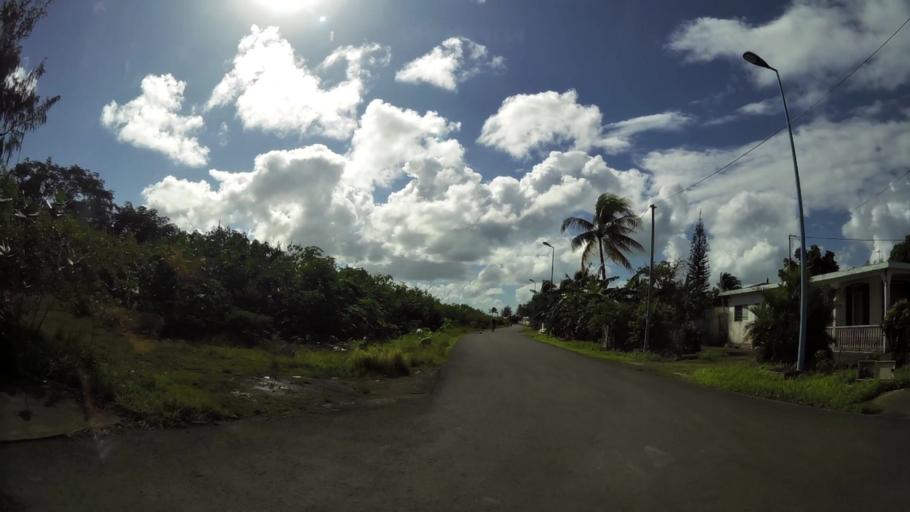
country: GP
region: Guadeloupe
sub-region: Guadeloupe
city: Port-Louis
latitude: 16.4151
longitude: -61.5311
